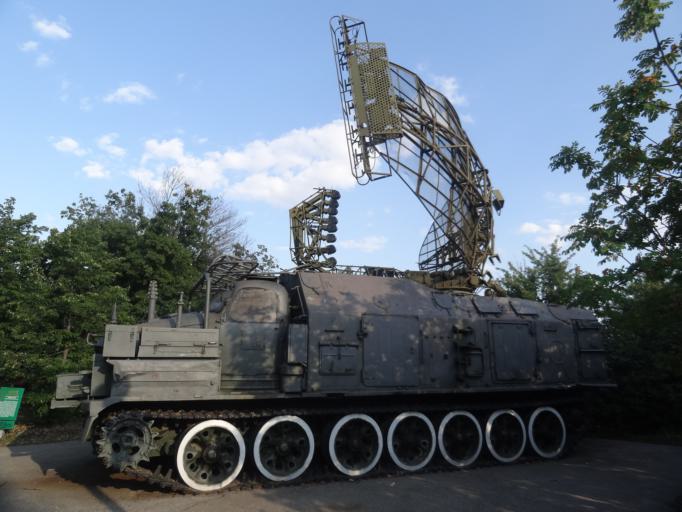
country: RU
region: Saratov
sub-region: Saratovskiy Rayon
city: Saratov
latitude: 51.5423
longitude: 46.0572
